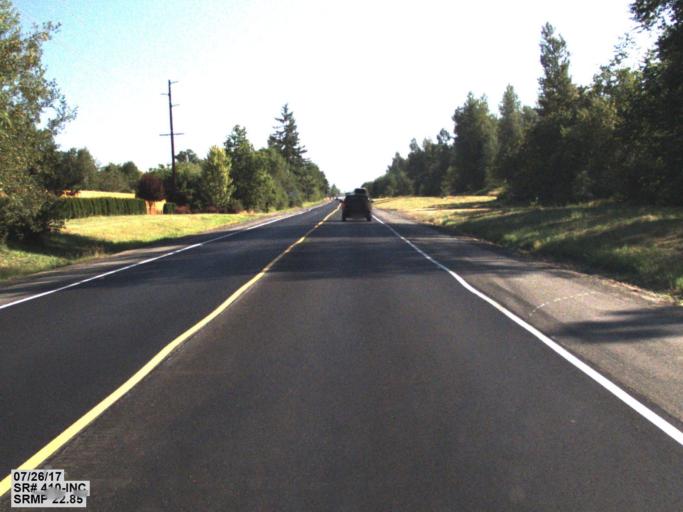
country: US
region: Washington
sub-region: Pierce County
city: Buckley
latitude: 47.1822
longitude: -122.0104
